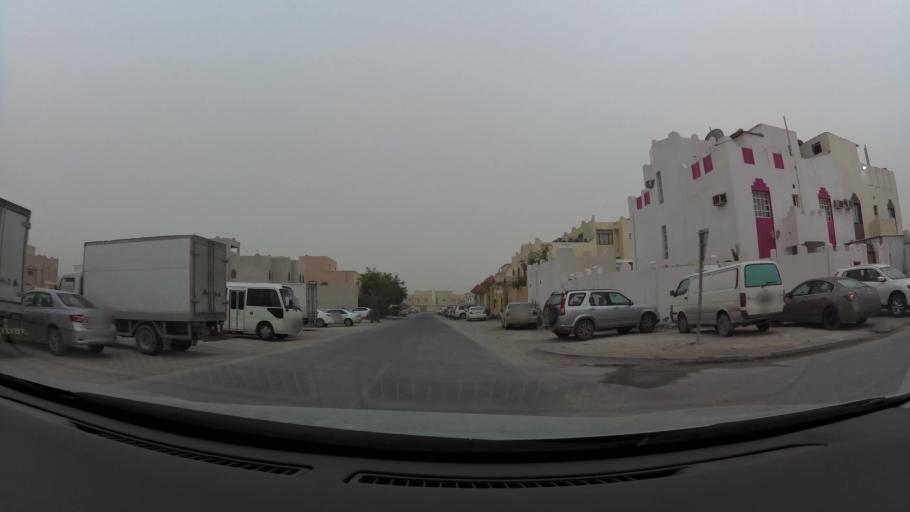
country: QA
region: Baladiyat ad Dawhah
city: Doha
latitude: 25.2408
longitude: 51.4882
